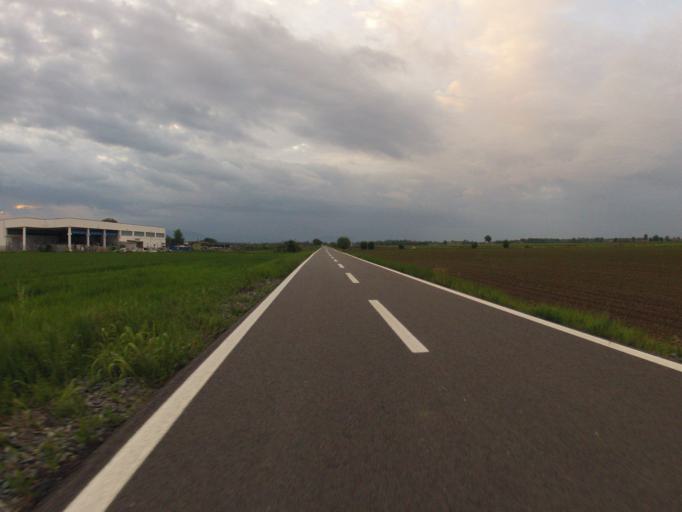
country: IT
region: Piedmont
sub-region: Provincia di Torino
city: Villafranca Piemonte
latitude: 44.7923
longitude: 7.5077
